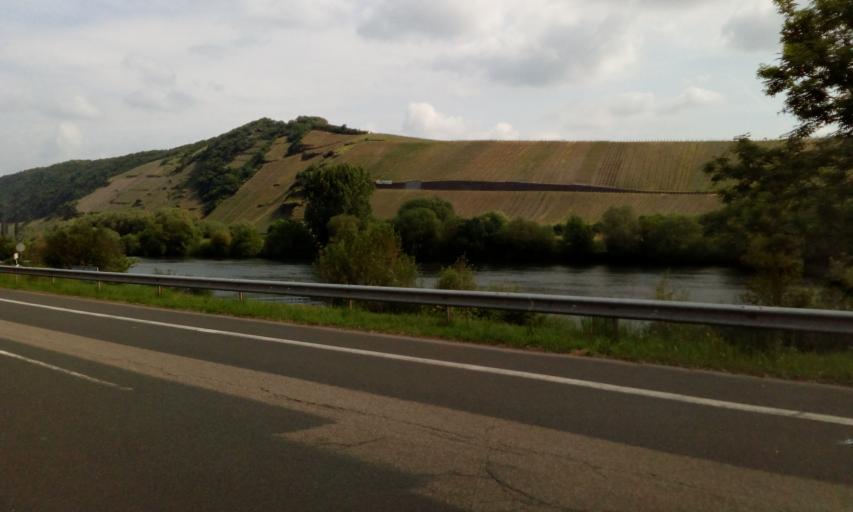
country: DE
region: Rheinland-Pfalz
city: Leiwen
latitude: 49.8211
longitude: 6.8841
